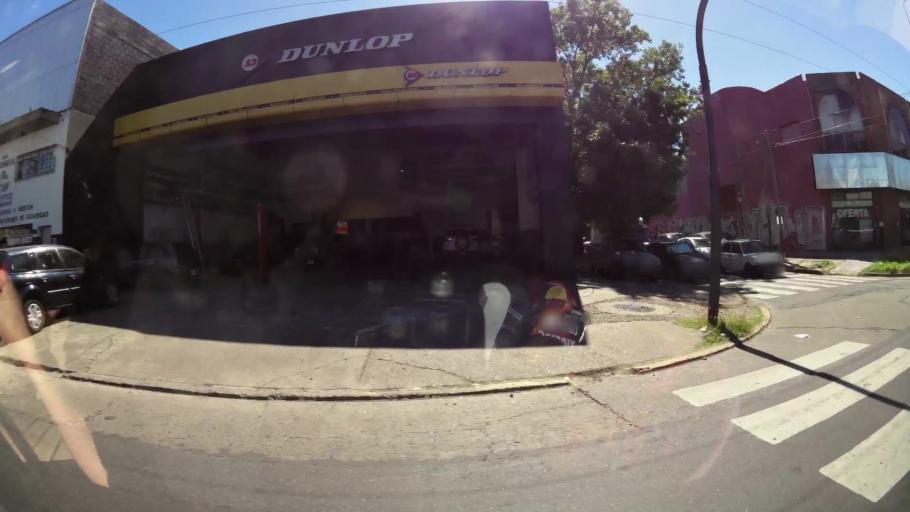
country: AR
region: Buenos Aires
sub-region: Partido de Vicente Lopez
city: Olivos
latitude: -34.5202
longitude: -58.5239
